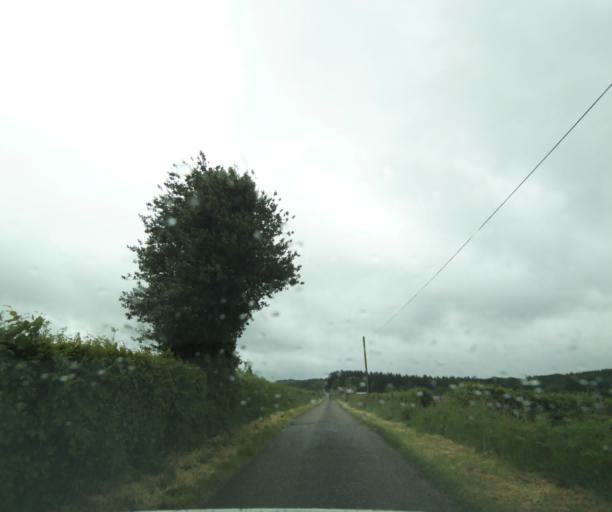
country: FR
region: Bourgogne
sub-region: Departement de Saone-et-Loire
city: Charolles
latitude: 46.4833
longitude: 4.4152
